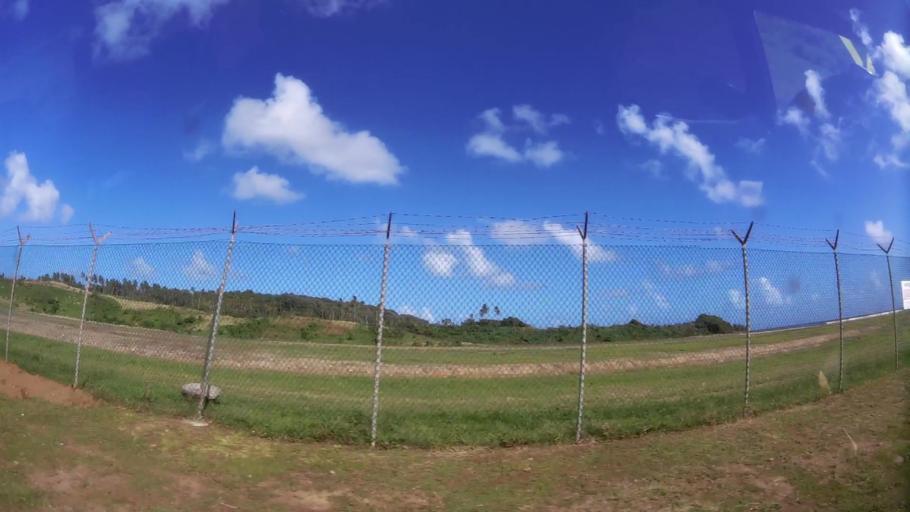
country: DM
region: Saint Andrew
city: Marigot
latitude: 15.5472
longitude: -61.2967
